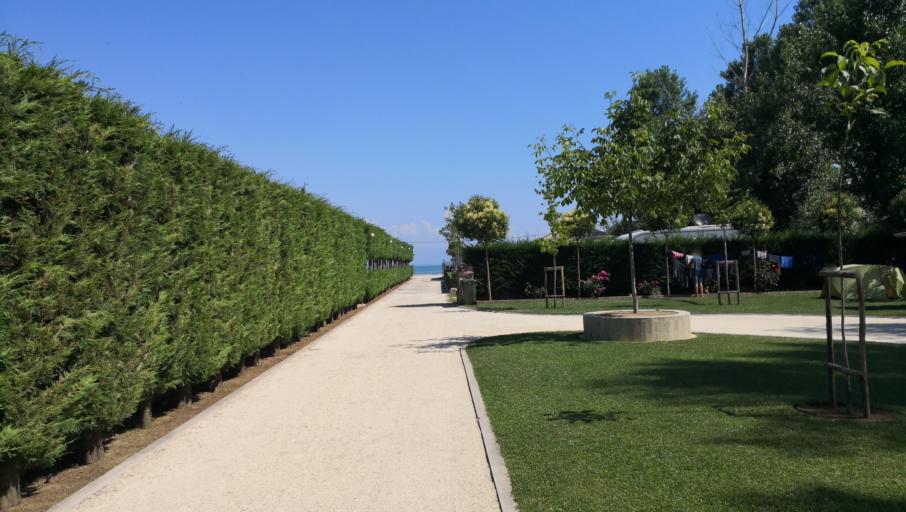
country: AL
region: Korce
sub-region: Rrethi i Pogradecit
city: Bucimas
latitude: 40.9006
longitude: 20.7098
